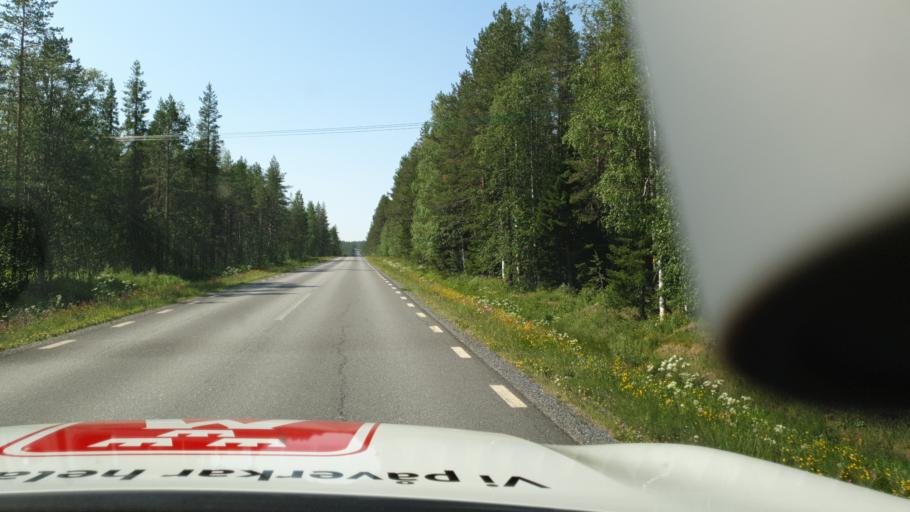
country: SE
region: Vaesterbotten
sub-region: Skelleftea Kommun
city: Langsele
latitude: 64.9861
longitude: 20.0771
